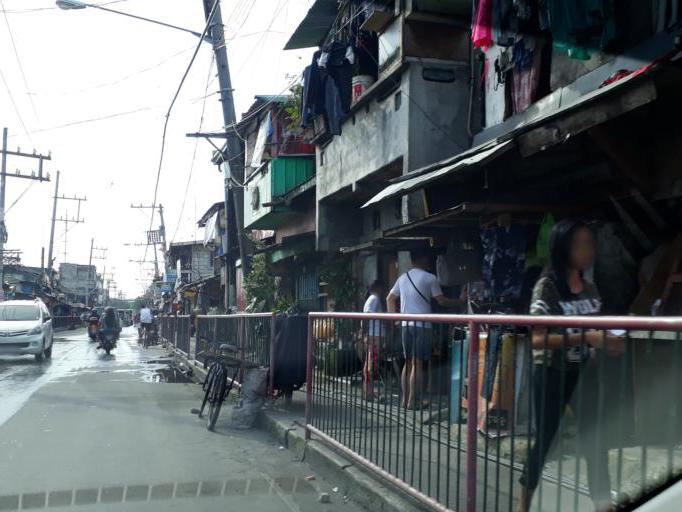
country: PH
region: Metro Manila
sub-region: Caloocan City
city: Niugan
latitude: 14.6683
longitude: 120.9636
